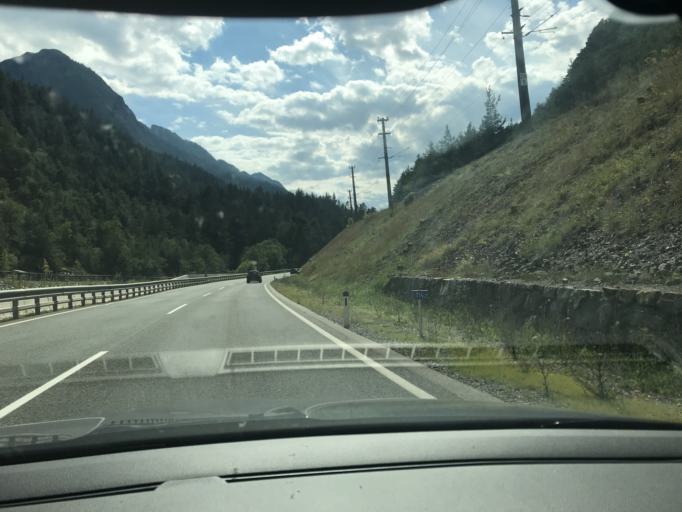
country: AT
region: Tyrol
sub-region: Politischer Bezirk Lienz
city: Leisach
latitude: 46.7926
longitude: 12.7194
